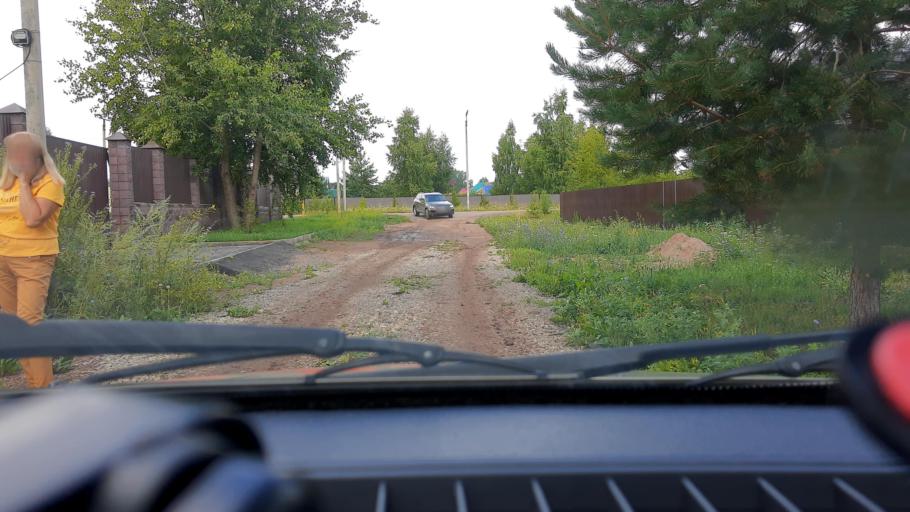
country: RU
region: Bashkortostan
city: Ufa
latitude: 54.6556
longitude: 56.0553
